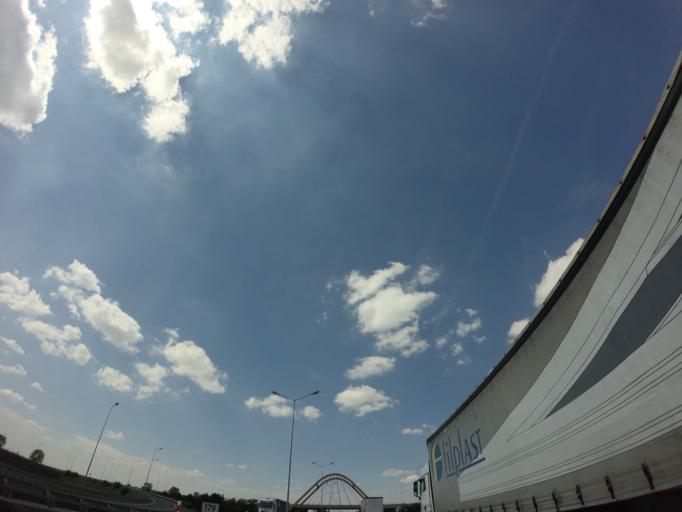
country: PL
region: Lower Silesian Voivodeship
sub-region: Powiat strzelinski
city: Wiazow
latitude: 50.8774
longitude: 17.2045
